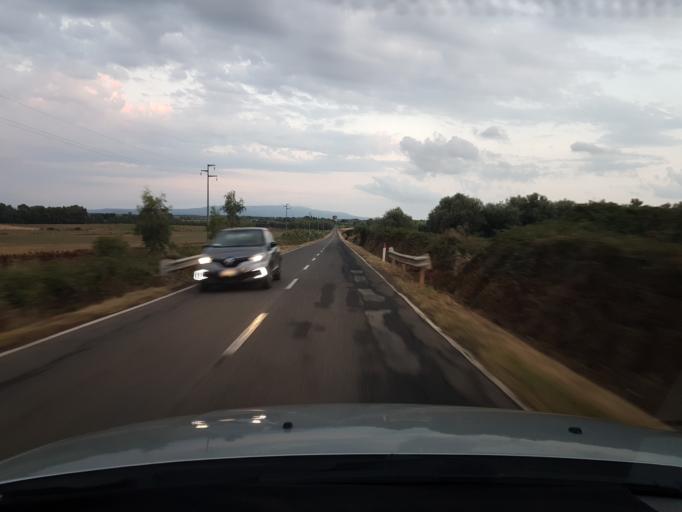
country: IT
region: Sardinia
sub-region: Provincia di Oristano
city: Tramatza
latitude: 40.0182
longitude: 8.6434
